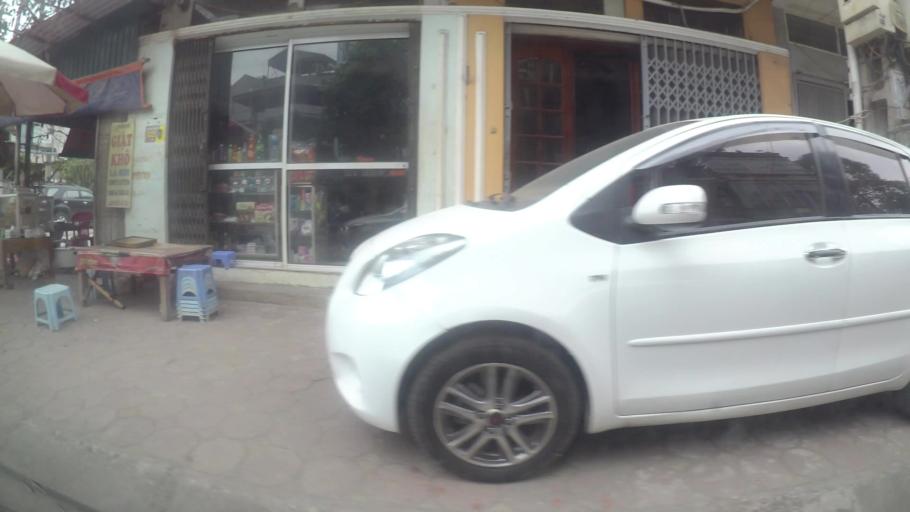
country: VN
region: Ha Noi
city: Ha Dong
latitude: 20.9710
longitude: 105.7708
